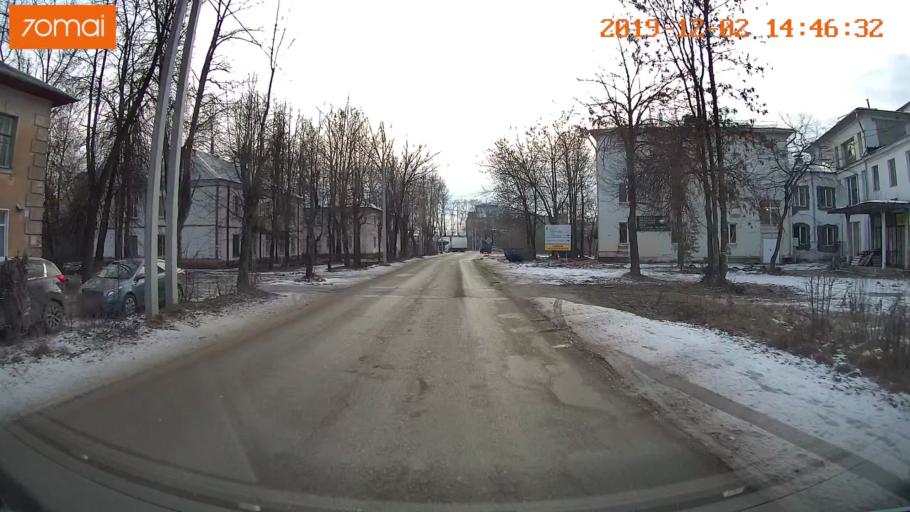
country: RU
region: Ivanovo
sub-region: Gorod Ivanovo
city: Ivanovo
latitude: 56.9877
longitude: 41.0252
